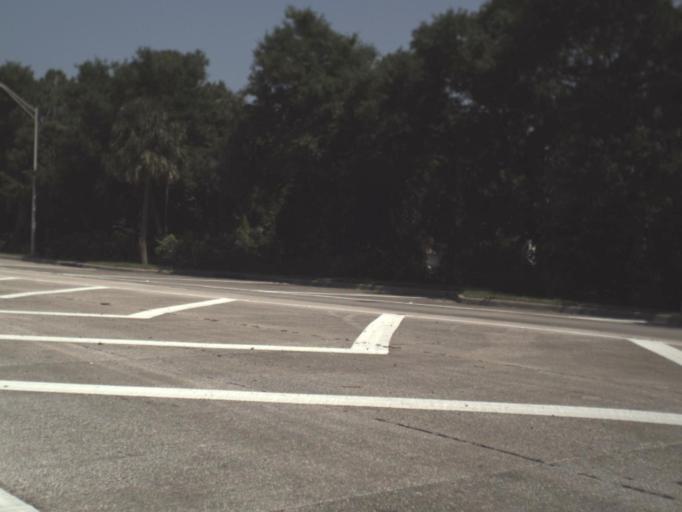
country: US
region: Florida
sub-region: Duval County
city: Jacksonville
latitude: 30.3089
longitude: -81.6204
